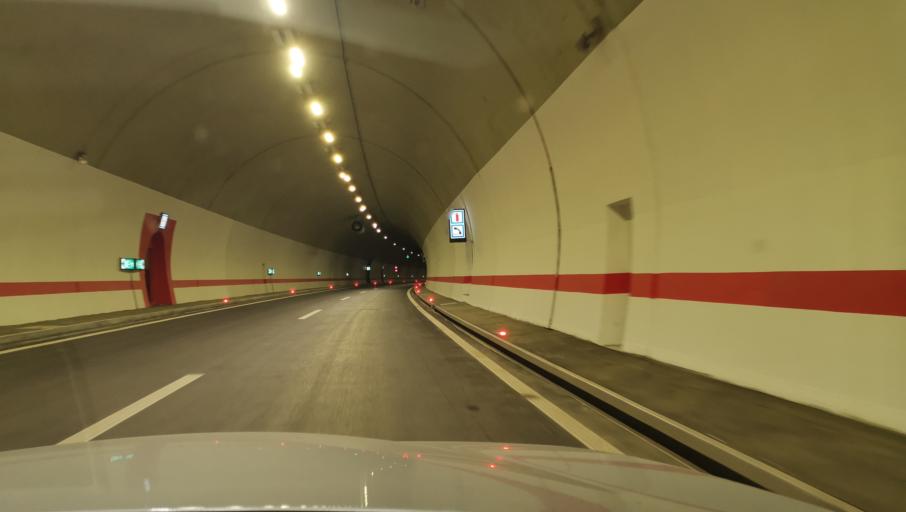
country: RS
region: Central Serbia
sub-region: Kolubarski Okrug
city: Ljig
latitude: 44.2039
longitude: 20.2652
